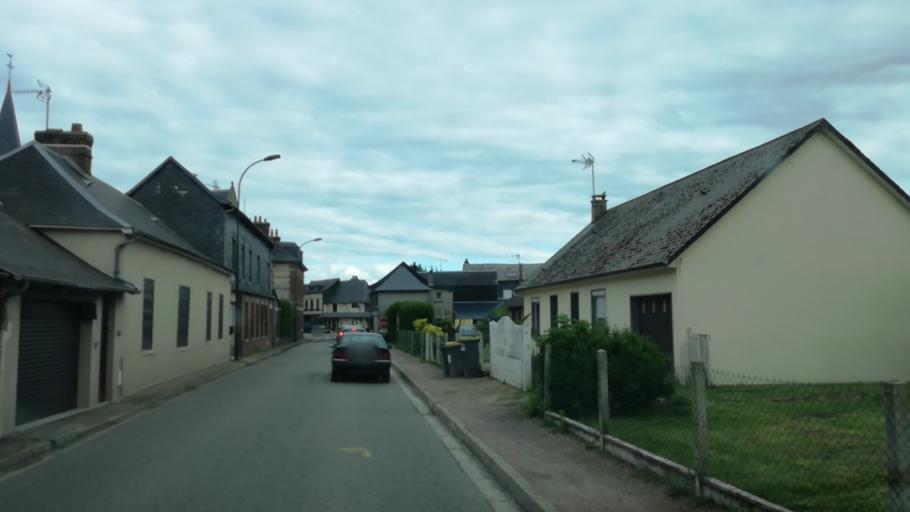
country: FR
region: Haute-Normandie
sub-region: Departement de l'Eure
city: Bourgtheroulde-Infreville
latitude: 49.2271
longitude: 0.8408
